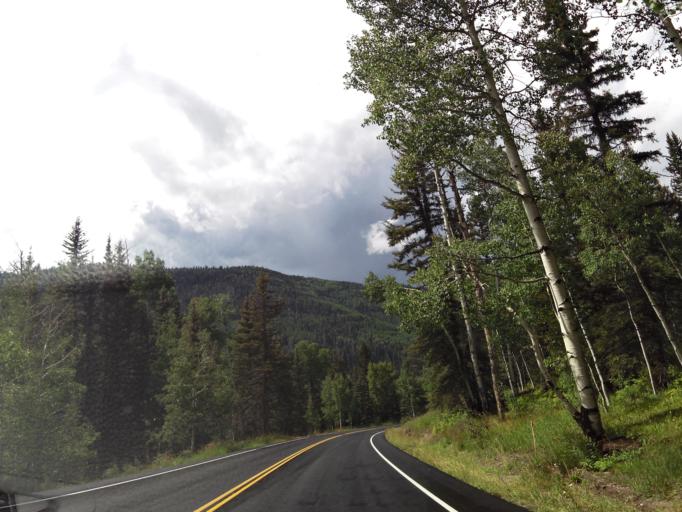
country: US
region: Colorado
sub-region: San Juan County
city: Silverton
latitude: 37.6564
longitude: -107.8038
